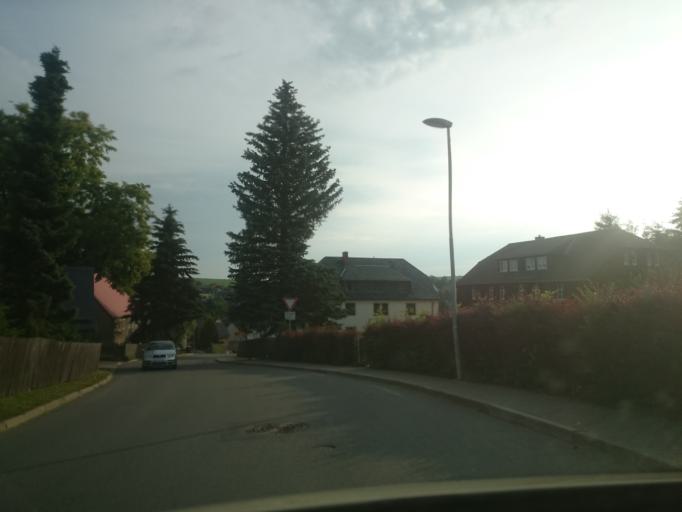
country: DE
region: Saxony
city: Leubsdorf
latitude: 50.7988
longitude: 13.1661
